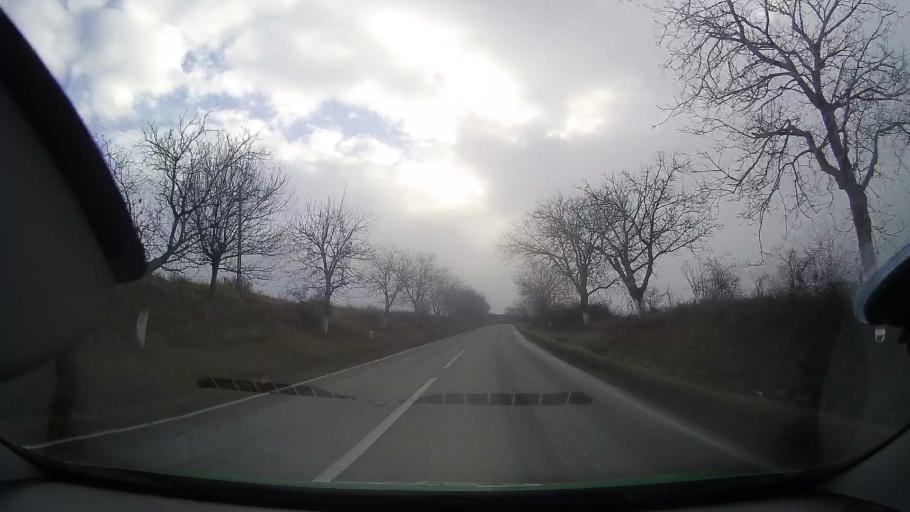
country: RO
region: Mures
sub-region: Municipiul Tarnaveni
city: Bobohalma
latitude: 46.3574
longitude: 24.2672
